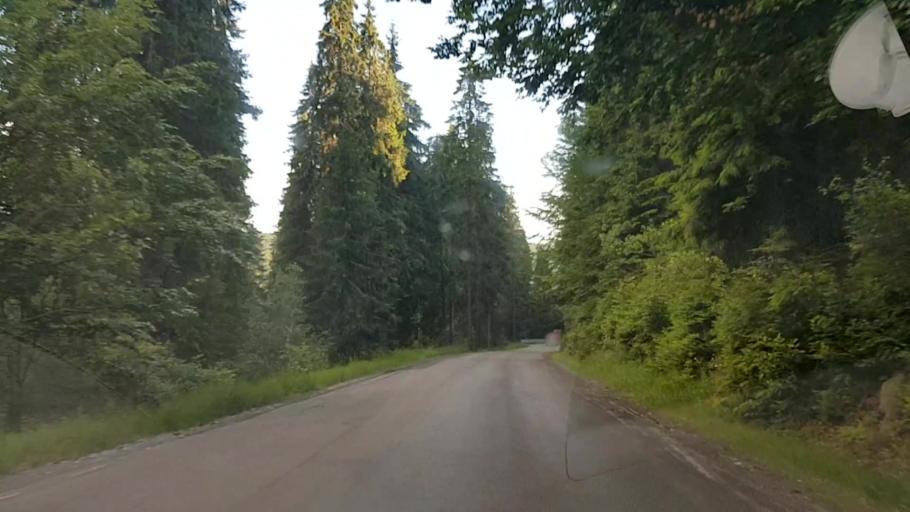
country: RO
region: Harghita
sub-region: Comuna Varsag
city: Varsag
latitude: 46.6481
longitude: 25.2883
